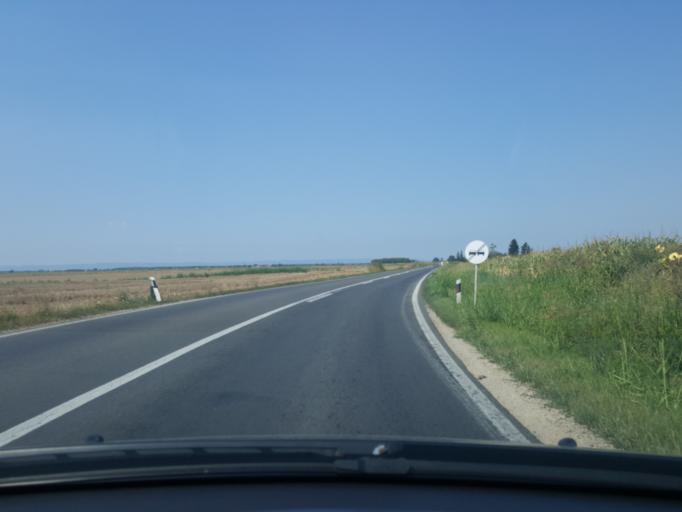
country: RS
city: Platicevo
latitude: 44.8442
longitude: 19.7670
